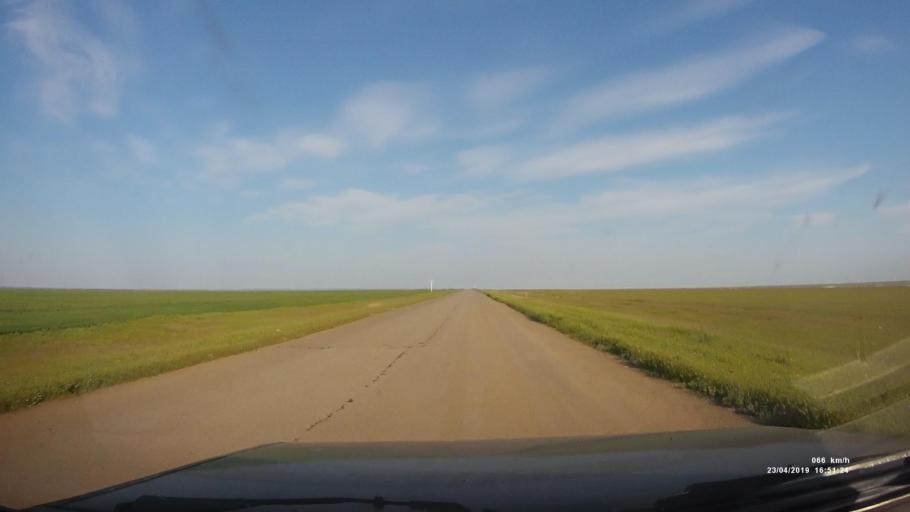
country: RU
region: Kalmykiya
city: Priyutnoye
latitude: 46.3232
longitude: 43.3056
